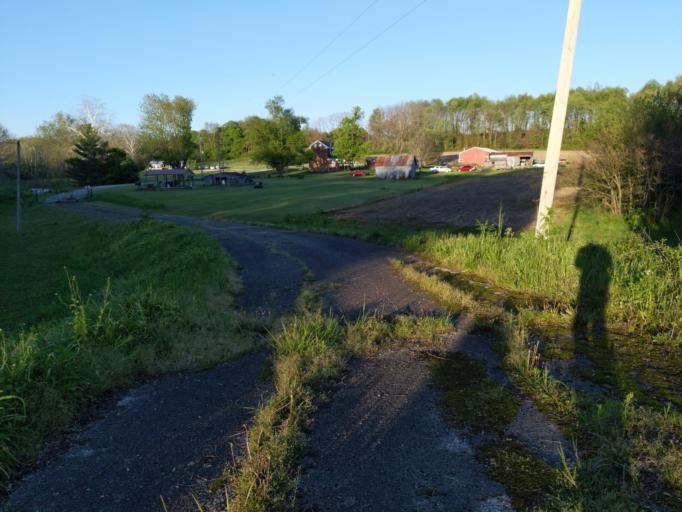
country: US
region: Indiana
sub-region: Decatur County
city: Westport
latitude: 39.1900
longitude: -85.4353
